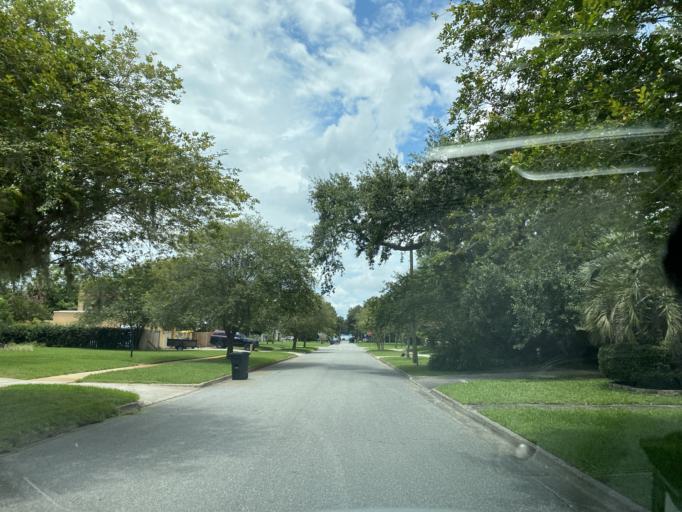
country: US
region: Florida
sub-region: Seminole County
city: Sanford
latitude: 28.8090
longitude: -81.2515
